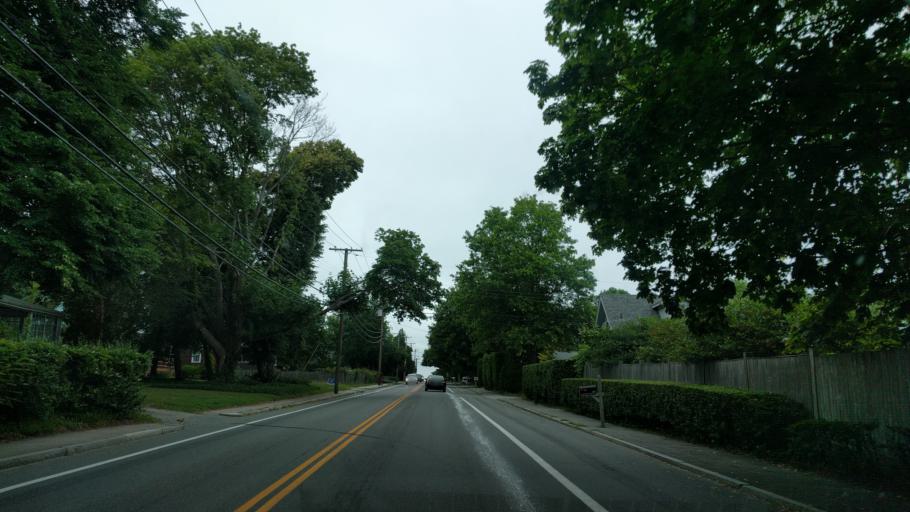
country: US
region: Rhode Island
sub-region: Newport County
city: Jamestown
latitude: 41.5027
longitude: -71.3645
